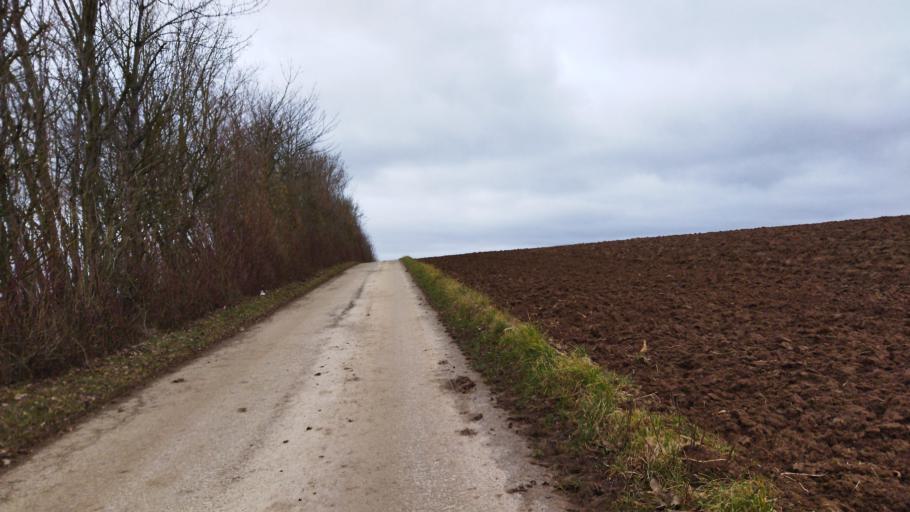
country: DE
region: Baden-Wuerttemberg
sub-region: Regierungsbezirk Stuttgart
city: Ilsfeld
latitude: 49.0763
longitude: 9.2498
